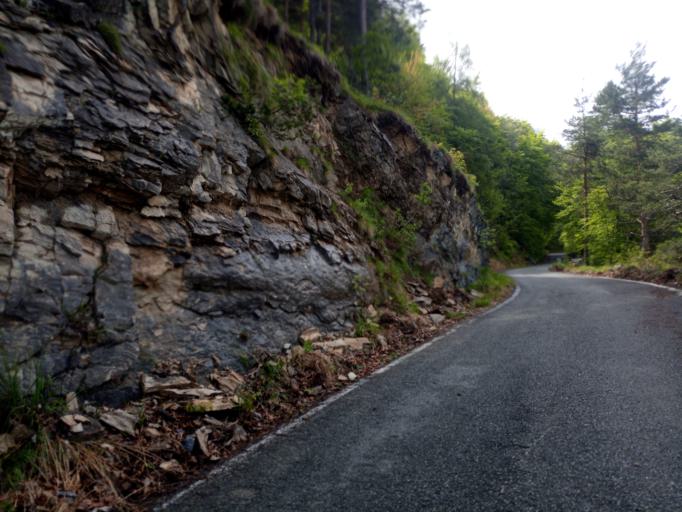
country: IT
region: Piedmont
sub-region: Provincia di Torino
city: Meana di Susa
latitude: 45.1051
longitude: 7.0654
